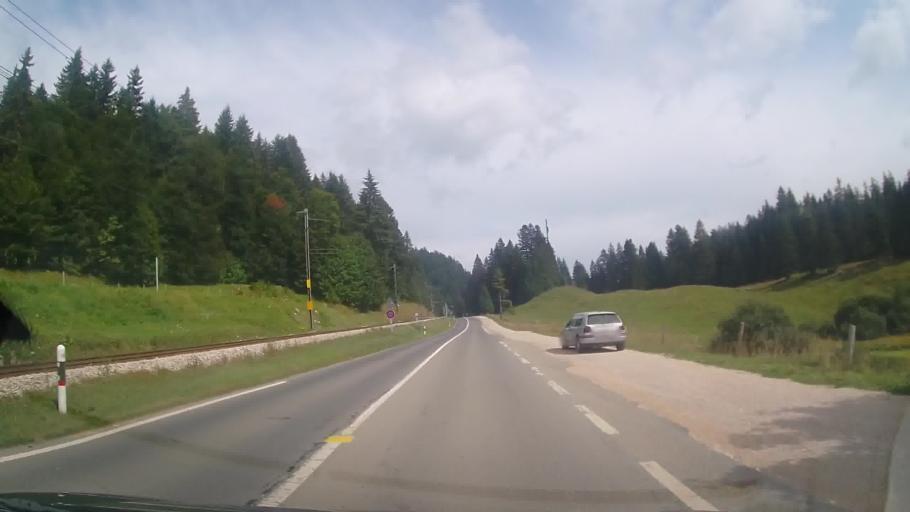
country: CH
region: Vaud
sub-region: Nyon District
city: Saint-Cergue
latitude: 46.4545
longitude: 6.1126
